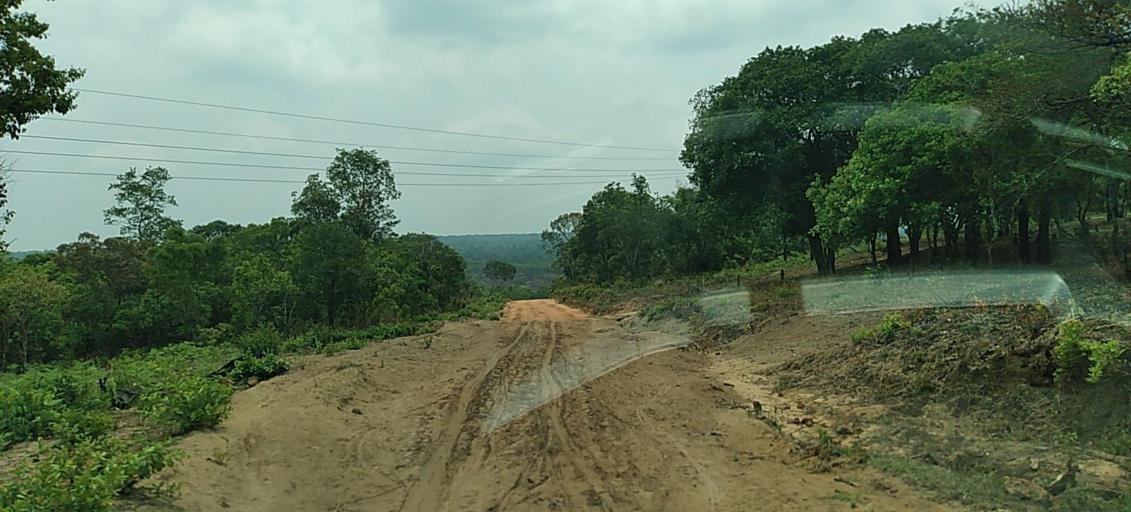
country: ZM
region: North-Western
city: Mwinilunga
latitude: -11.4629
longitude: 24.7634
